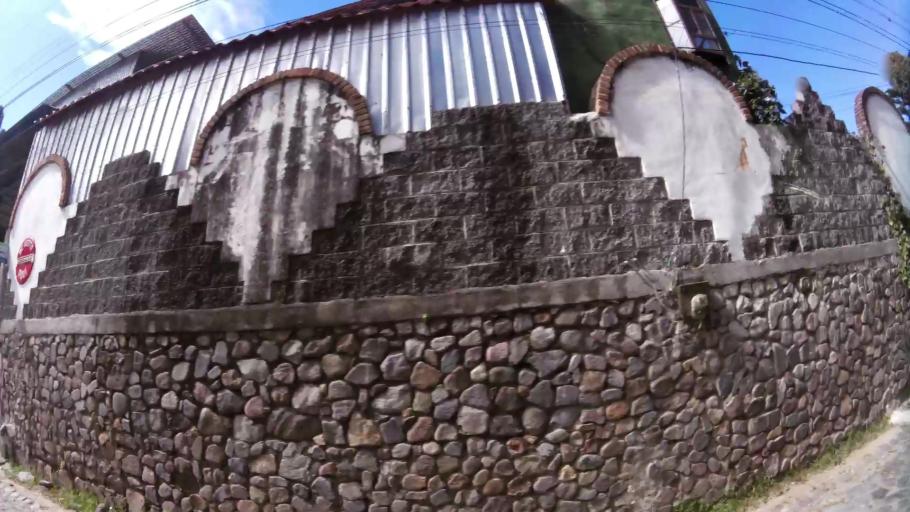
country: GT
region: Solola
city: Panajachel
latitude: 14.7425
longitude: -91.1548
